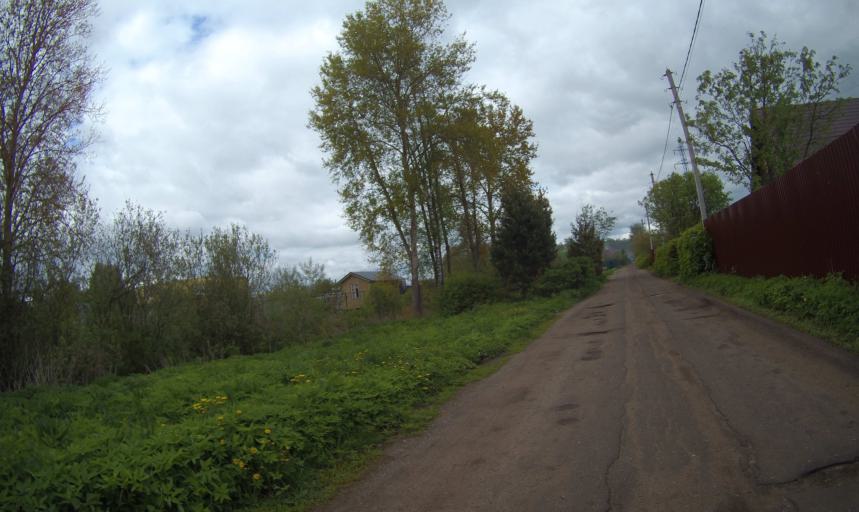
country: RU
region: Moskovskaya
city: Rechitsy
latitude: 55.5513
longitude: 38.4810
